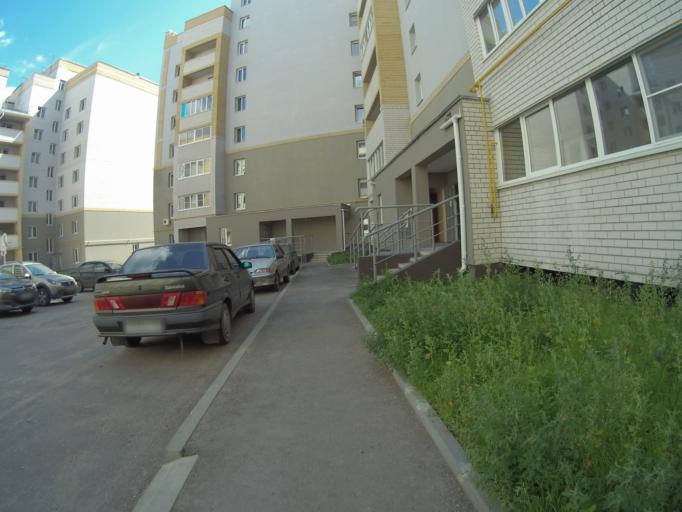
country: RU
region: Vladimir
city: Vladimir
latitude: 56.1382
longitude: 40.4139
